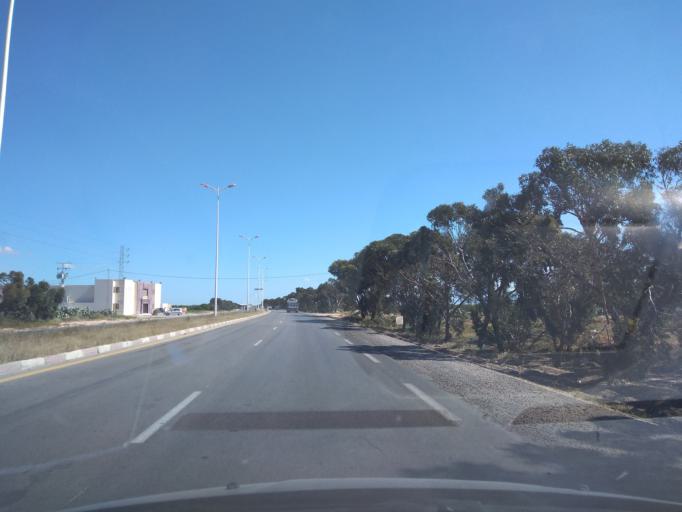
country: TN
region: Safaqis
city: Sfax
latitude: 34.8226
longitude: 10.7120
